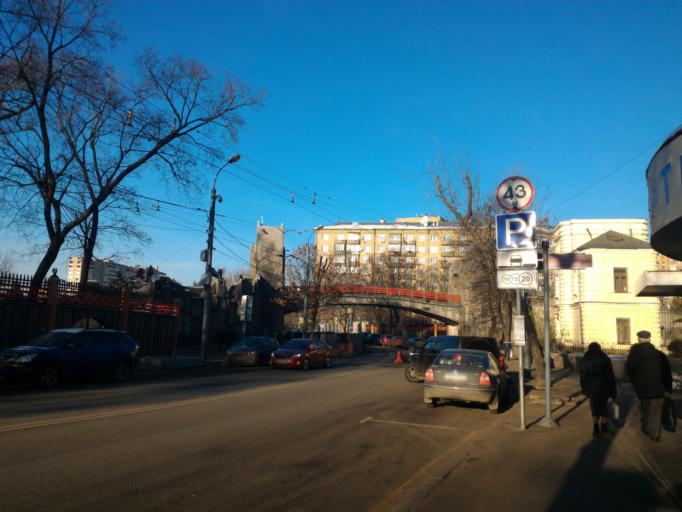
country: RU
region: Moskovskaya
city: Dorogomilovo
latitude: 55.7619
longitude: 37.5793
